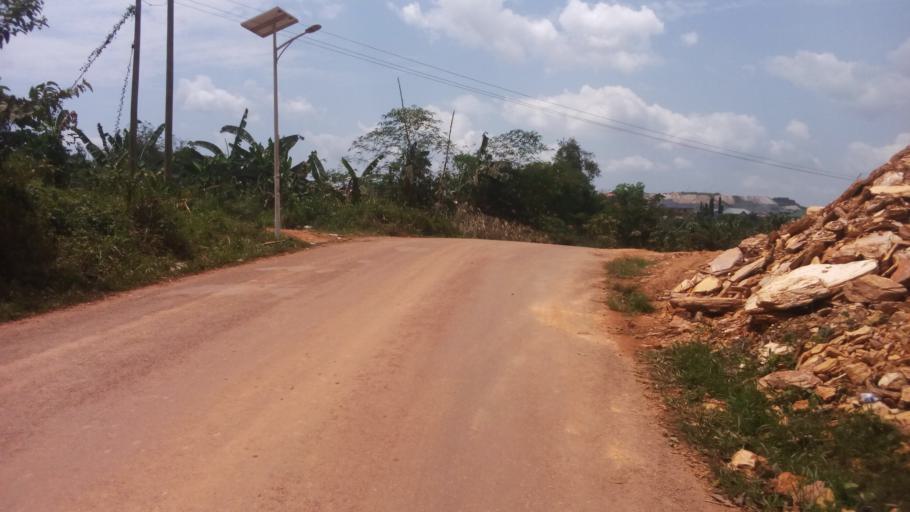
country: GH
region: Western
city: Tarkwa
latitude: 5.3023
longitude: -2.0020
